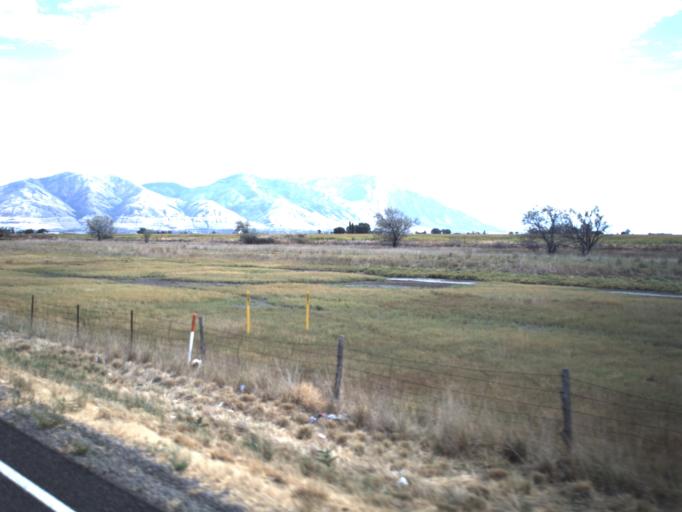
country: US
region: Utah
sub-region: Box Elder County
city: Honeyville
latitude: 41.5590
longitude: -112.1476
